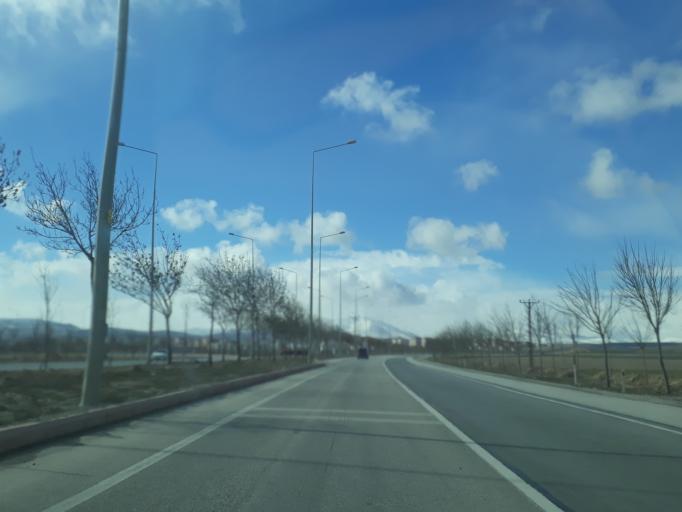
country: TR
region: Konya
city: Asagipinarbasi
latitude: 38.0050
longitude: 32.5553
